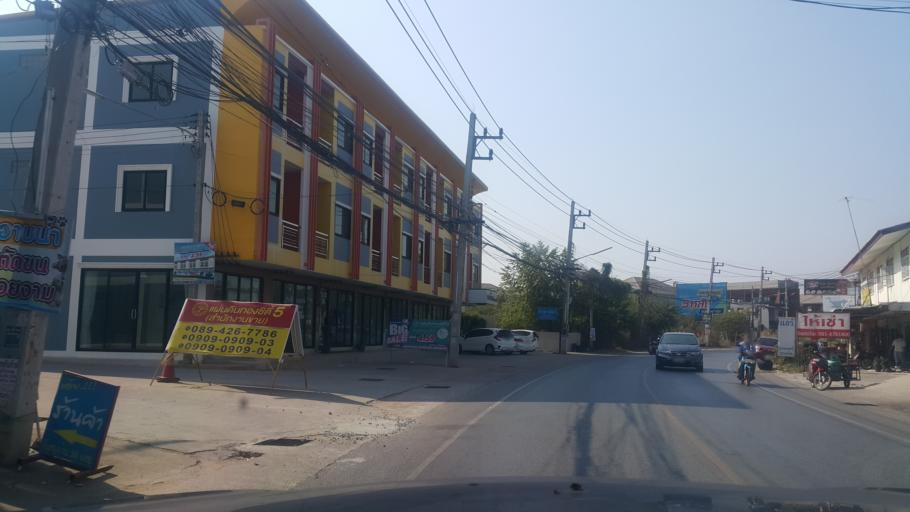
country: TH
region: Nakhon Ratchasima
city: Nakhon Ratchasima
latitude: 14.9427
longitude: 102.0419
